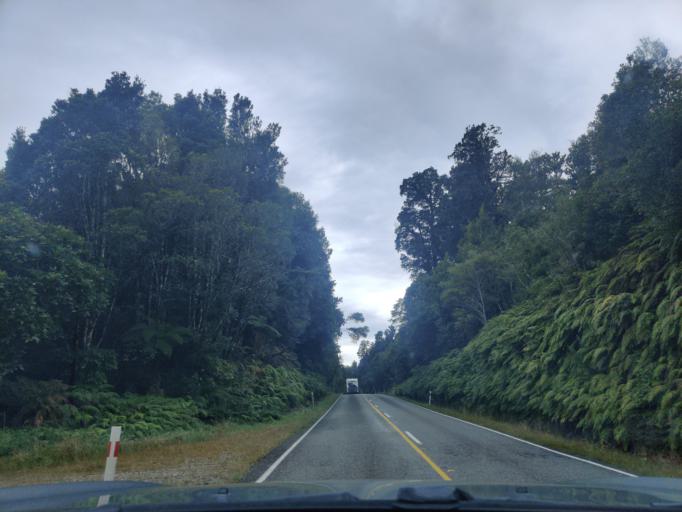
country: NZ
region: West Coast
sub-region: Westland District
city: Hokitika
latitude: -43.0306
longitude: 170.6568
